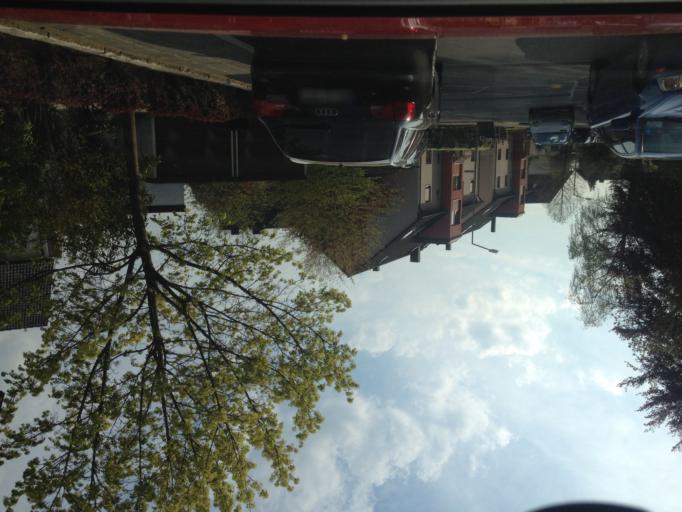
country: DE
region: Bavaria
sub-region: Regierungsbezirk Mittelfranken
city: Lauf an der Pegnitz
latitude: 49.5189
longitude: 11.2788
